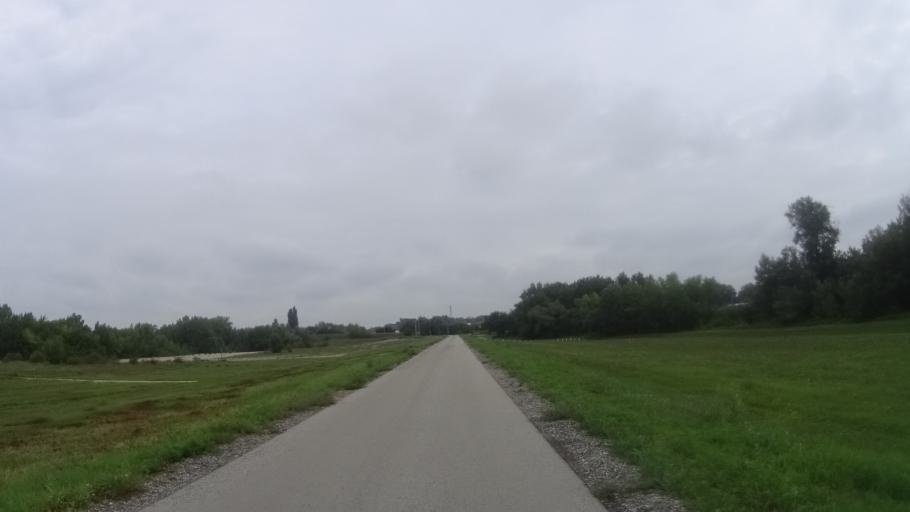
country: SK
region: Nitriansky
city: Komarno
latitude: 47.7587
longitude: 18.1460
